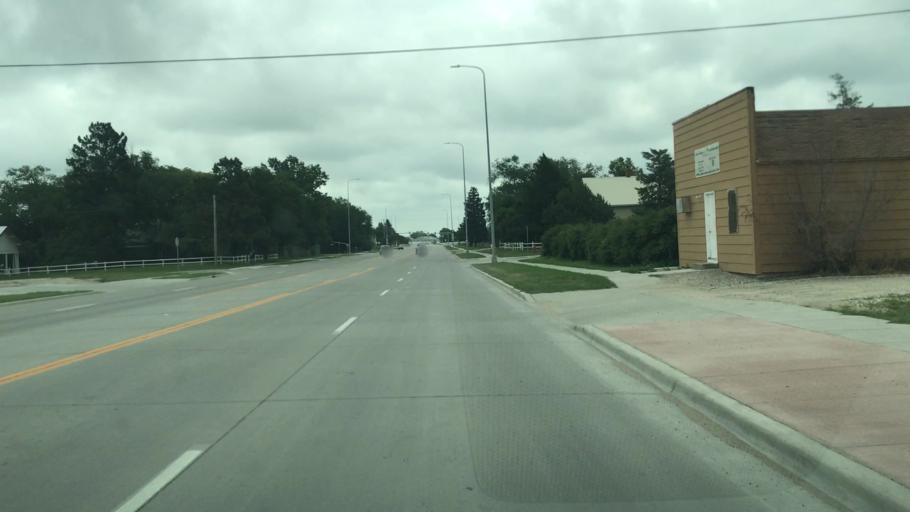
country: US
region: South Dakota
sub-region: Todd County
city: Mission
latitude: 43.3057
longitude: -100.6580
